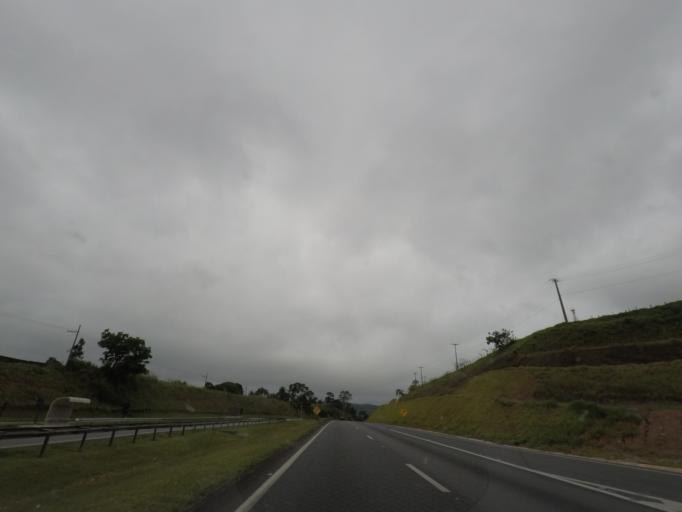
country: BR
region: Sao Paulo
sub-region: Bom Jesus Dos Perdoes
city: Bom Jesus dos Perdoes
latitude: -23.1666
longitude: -46.4089
